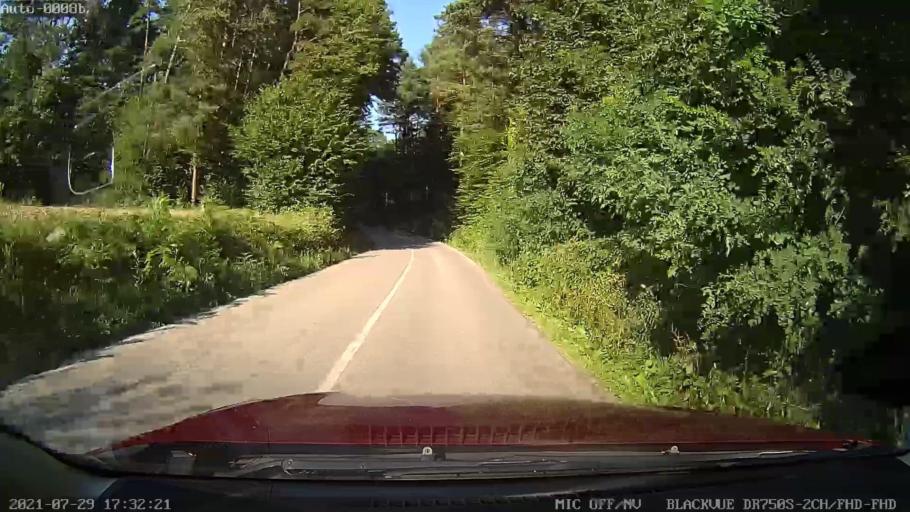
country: HR
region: Varazdinska
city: Vinica
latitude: 46.2914
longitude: 16.1302
